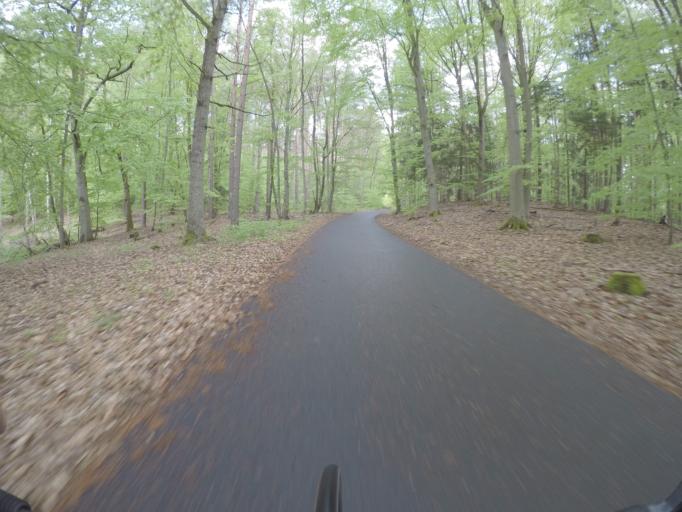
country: DE
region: Brandenburg
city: Marienwerder
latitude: 52.8634
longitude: 13.6138
